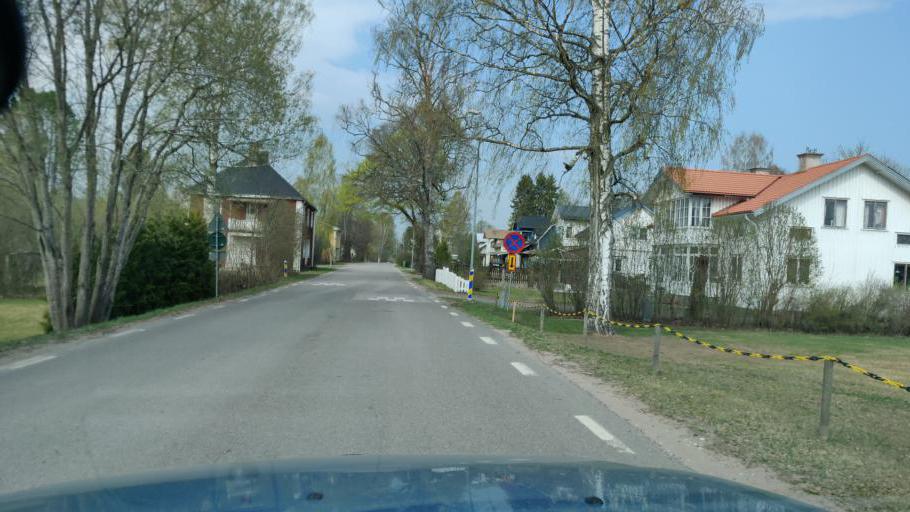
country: SE
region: Vaermland
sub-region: Munkfors Kommun
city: Munkfors
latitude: 59.8319
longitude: 13.5242
